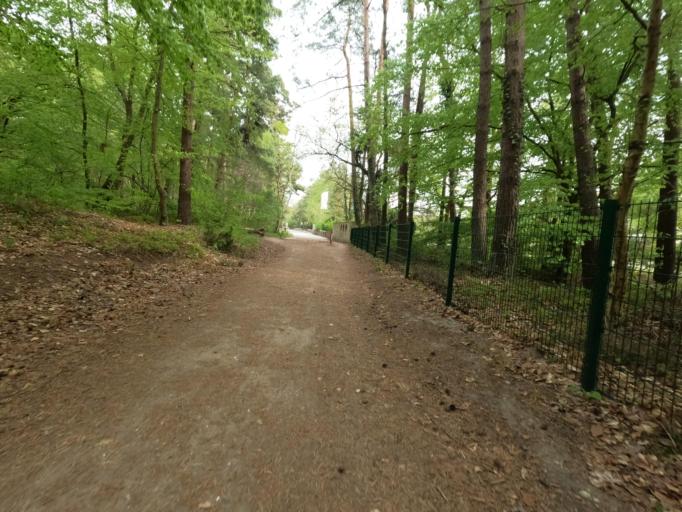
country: DE
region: Mecklenburg-Vorpommern
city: Ostseebad Prerow
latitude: 54.4457
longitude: 12.5476
